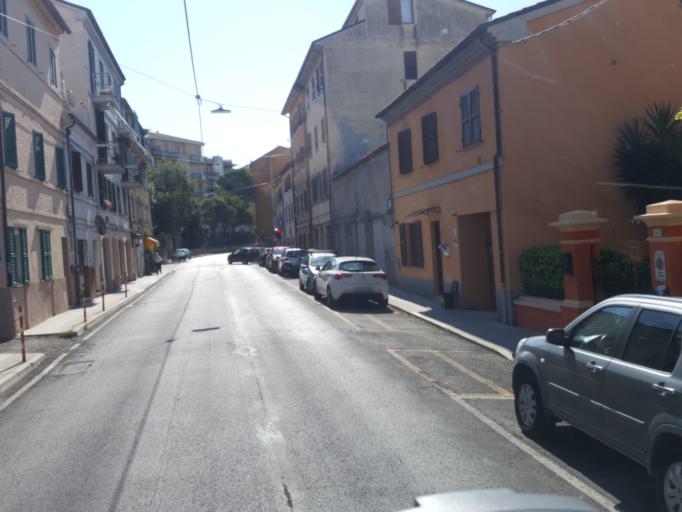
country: IT
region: The Marches
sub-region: Provincia di Ancona
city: Le Grazie di Ancona
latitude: 43.6020
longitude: 13.5143
